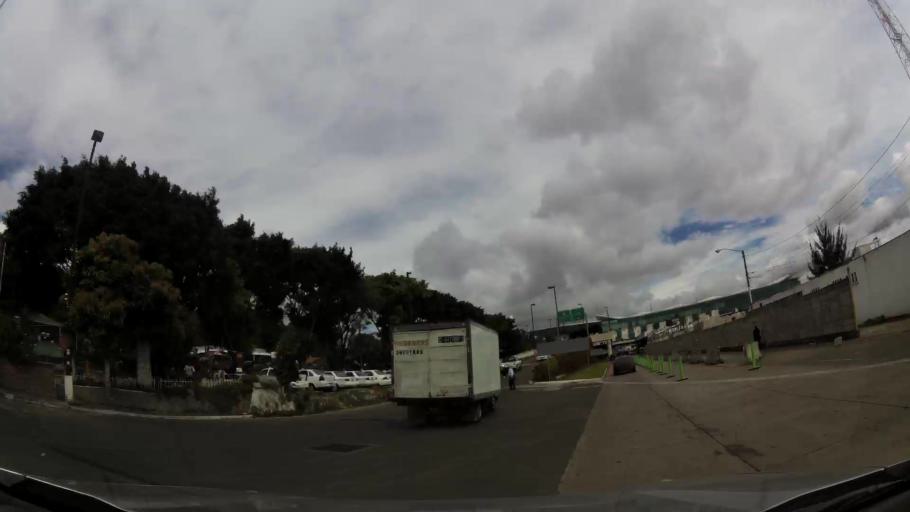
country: GT
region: Guatemala
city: Santa Catarina Pinula
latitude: 14.5866
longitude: -90.5312
